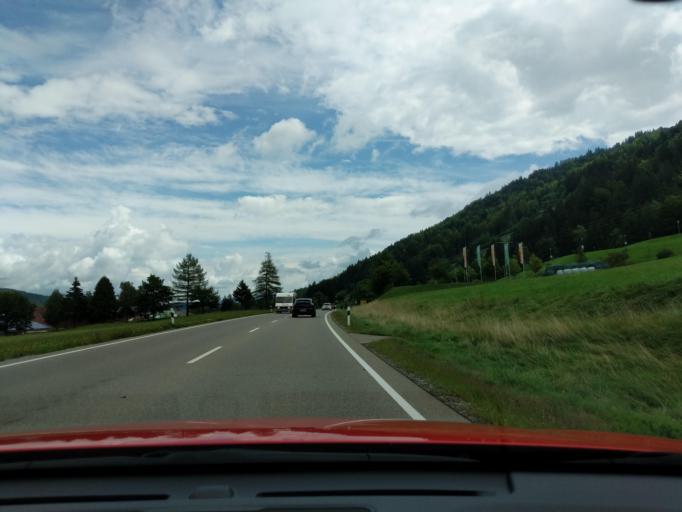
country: DE
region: Bavaria
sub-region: Swabia
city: Missen-Wilhams
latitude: 47.5604
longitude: 10.1329
